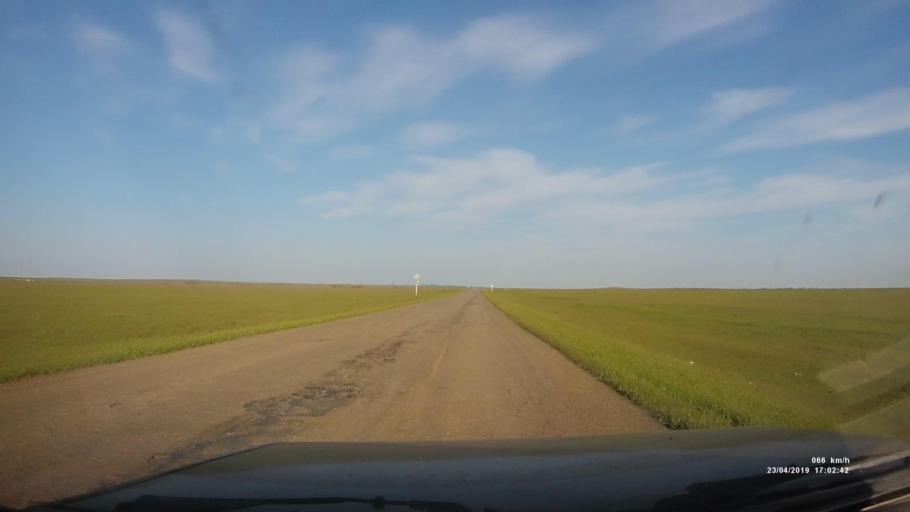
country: RU
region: Kalmykiya
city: Priyutnoye
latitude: 46.2919
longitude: 43.4211
